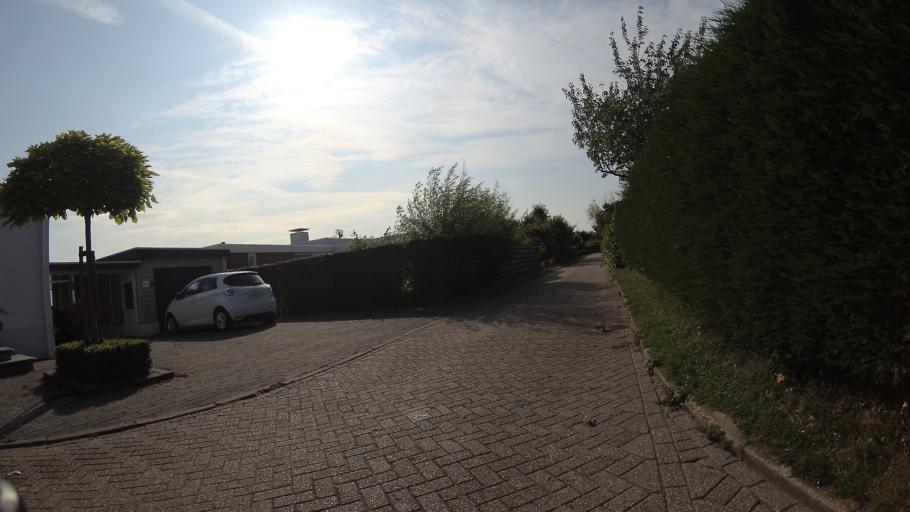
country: NL
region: Zeeland
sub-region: Gemeente Veere
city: Veere
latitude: 51.5670
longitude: 3.6680
